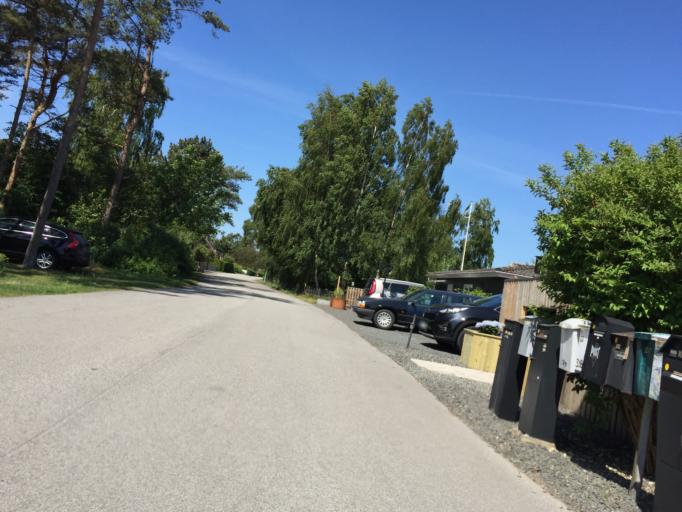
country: SE
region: Skane
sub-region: Trelleborgs Kommun
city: Anderslov
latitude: 55.3498
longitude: 13.2635
